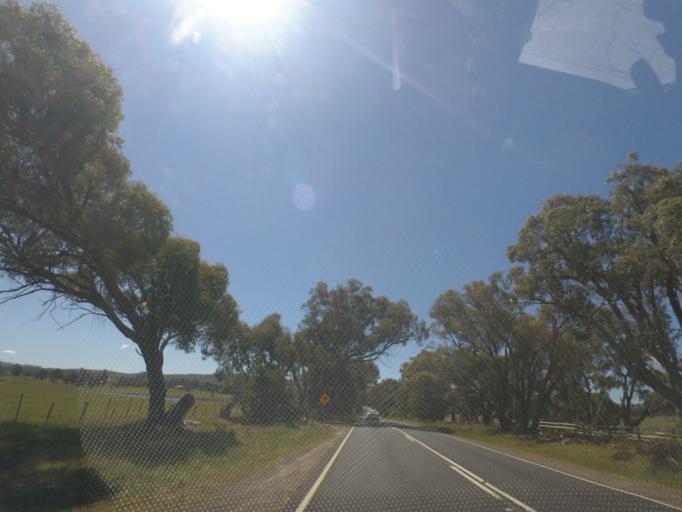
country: AU
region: Victoria
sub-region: Hume
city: Sunbury
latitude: -37.2516
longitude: 144.7389
